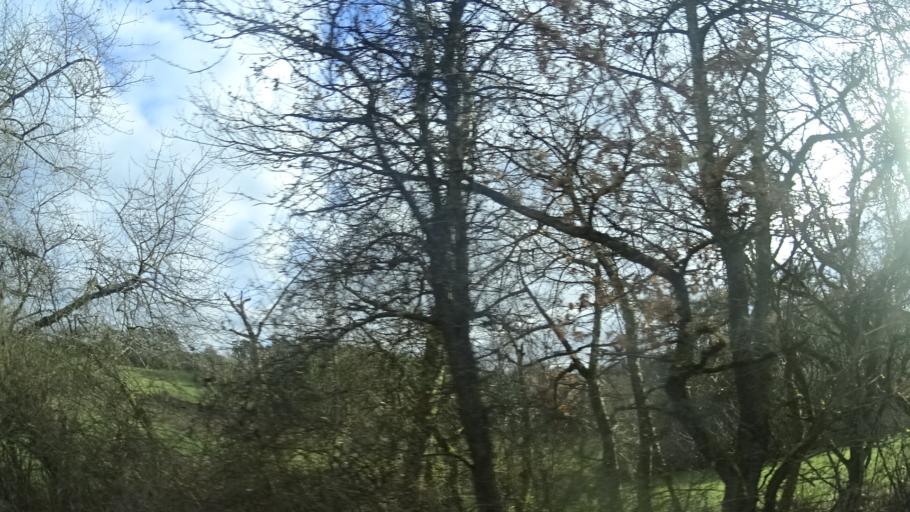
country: DE
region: Rheinland-Pfalz
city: Kronweiler
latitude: 49.6528
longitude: 7.2722
